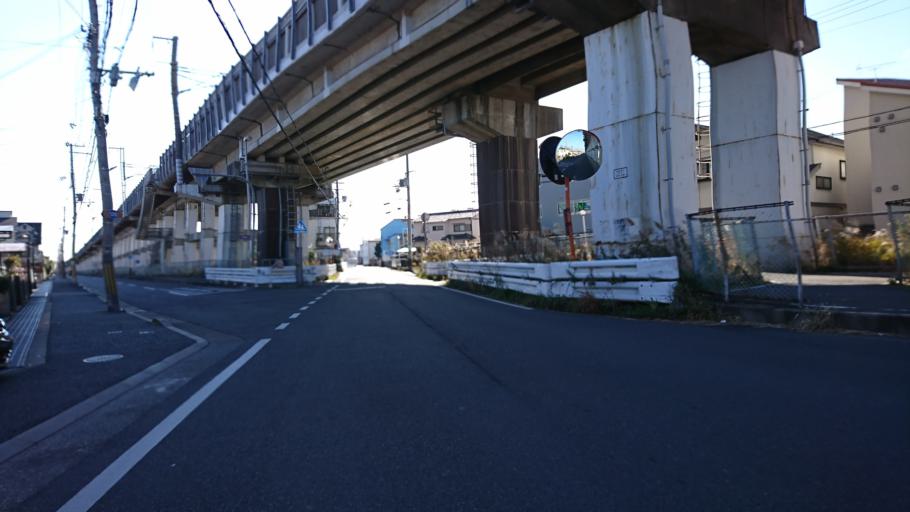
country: JP
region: Hyogo
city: Kakogawacho-honmachi
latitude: 34.7353
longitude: 134.8440
